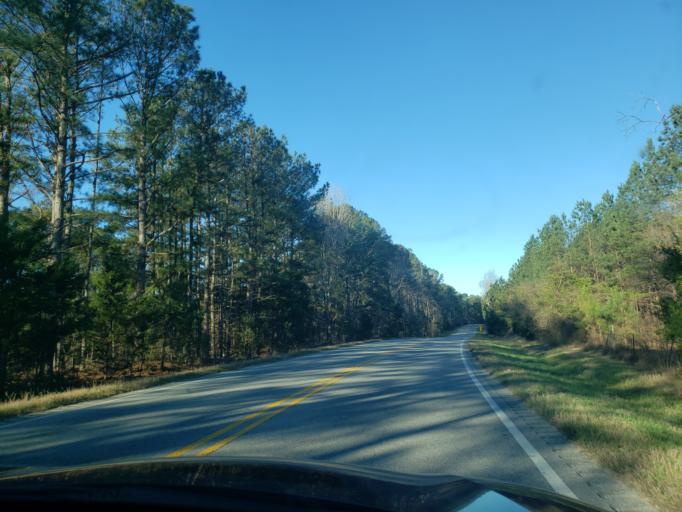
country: US
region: Alabama
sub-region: Lee County
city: Auburn
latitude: 32.5949
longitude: -85.6204
